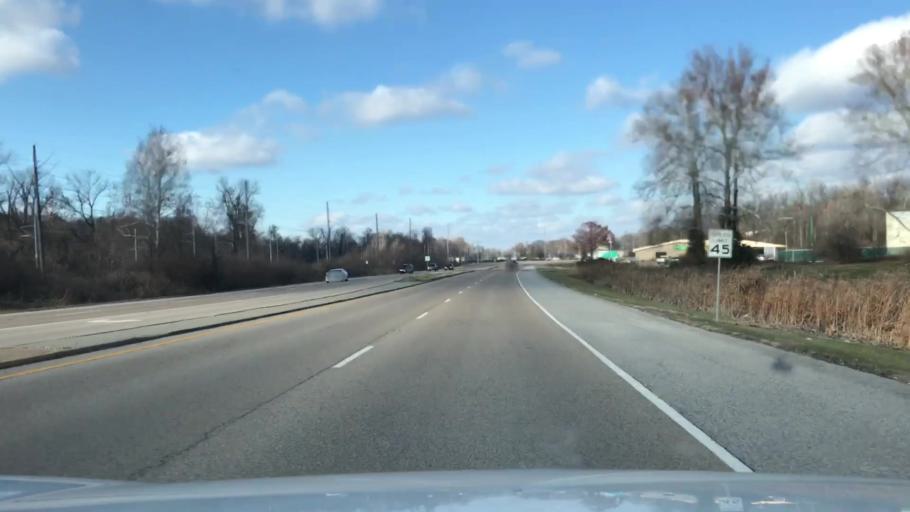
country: US
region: Illinois
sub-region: Saint Clair County
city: Caseyville
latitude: 38.5883
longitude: -90.0434
